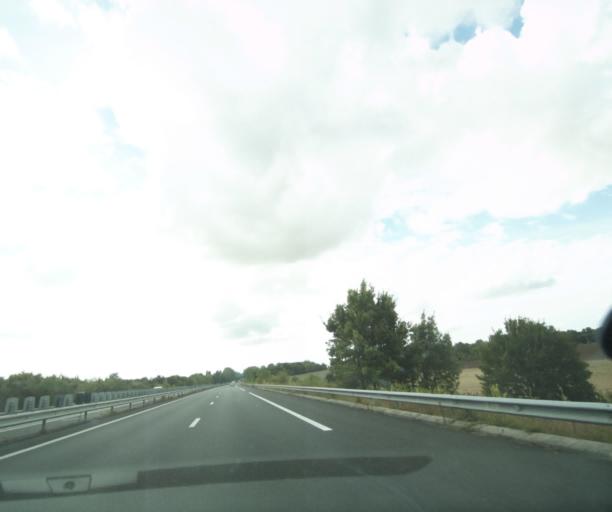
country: FR
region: Poitou-Charentes
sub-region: Departement de la Charente-Maritime
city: Chermignac
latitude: 45.7101
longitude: -0.6549
